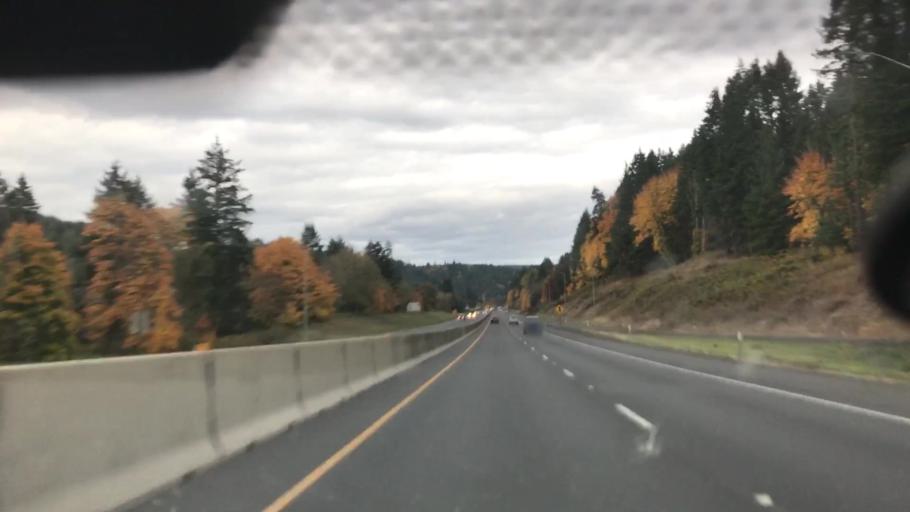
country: US
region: Oregon
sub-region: Douglas County
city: Drain
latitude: 43.7230
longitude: -123.2071
